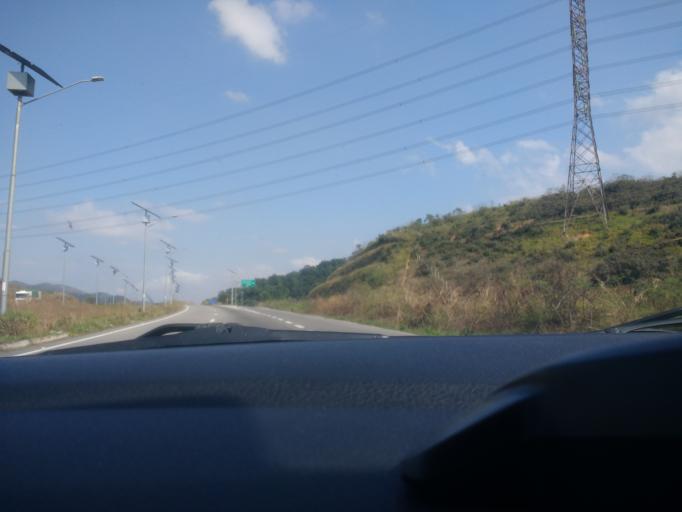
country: BR
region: Rio de Janeiro
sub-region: Nova Iguacu
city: Nova Iguacu
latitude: -22.6823
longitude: -43.4756
